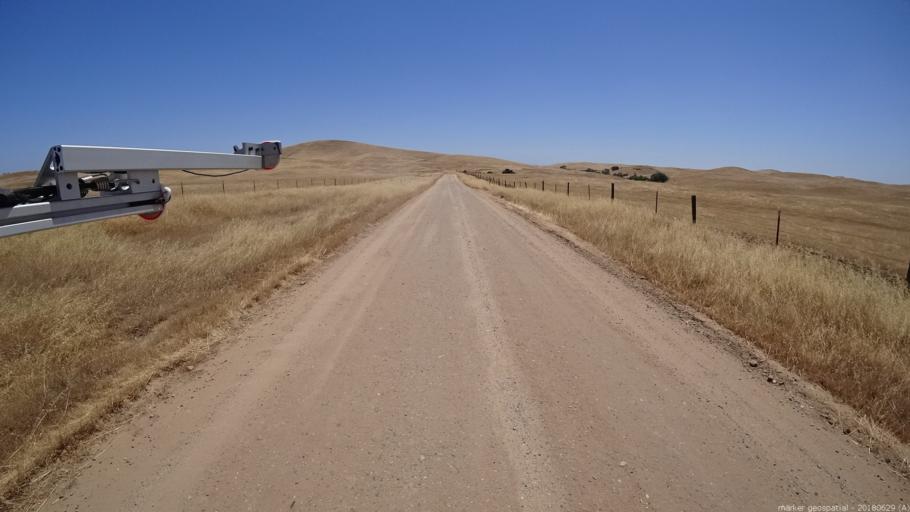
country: US
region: California
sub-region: Madera County
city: Bonadelle Ranchos-Madera Ranchos
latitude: 37.0803
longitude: -119.8837
